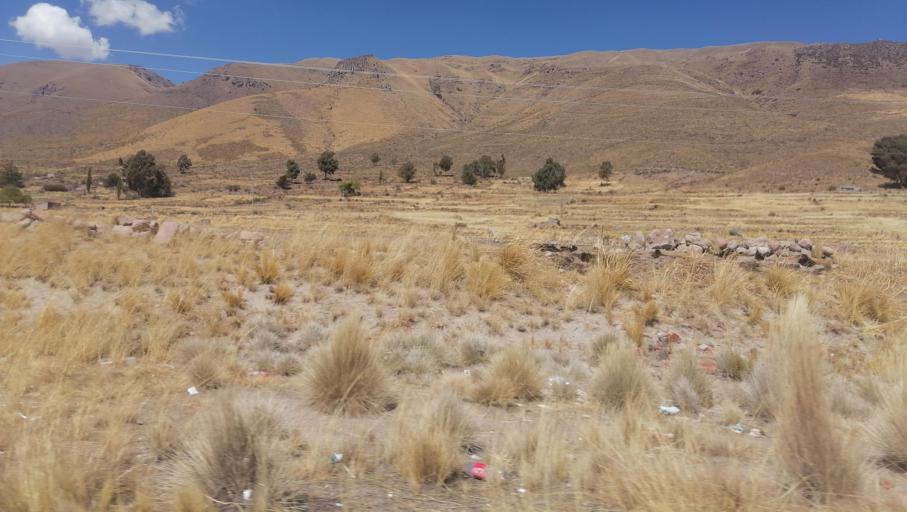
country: BO
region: Oruro
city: Challapata
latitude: -18.9893
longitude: -66.7788
